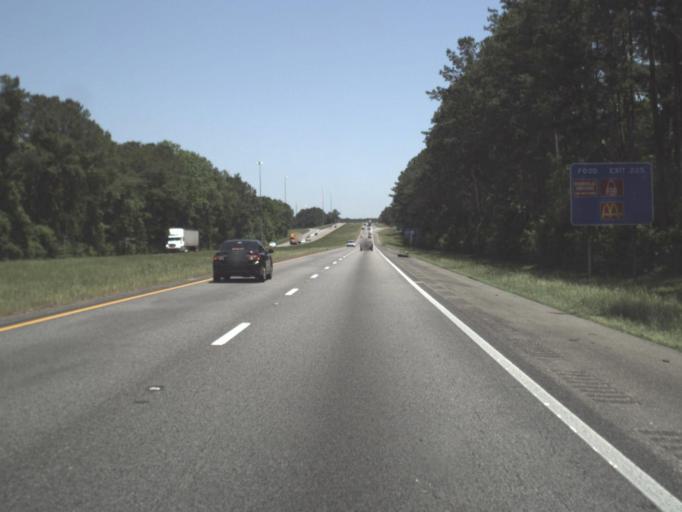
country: US
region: Florida
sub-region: Jefferson County
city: Monticello
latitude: 30.4776
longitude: -83.9015
